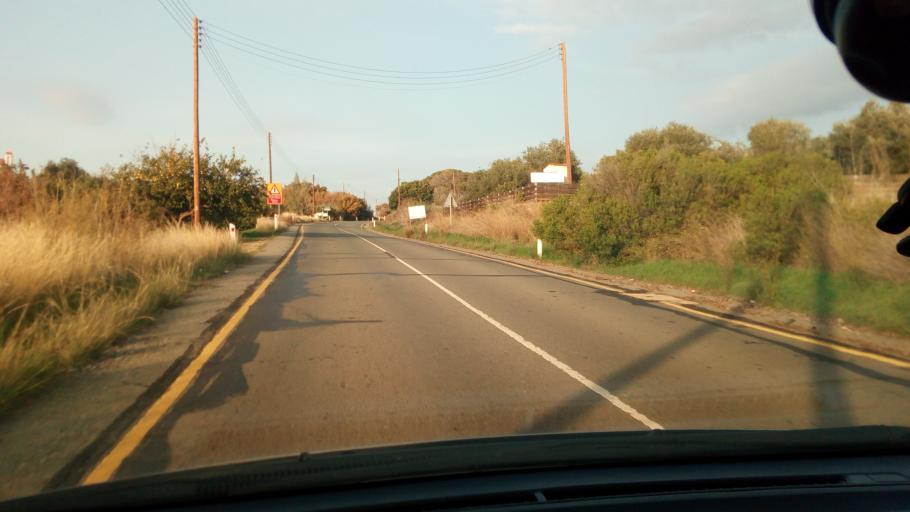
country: CY
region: Pafos
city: Polis
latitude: 35.1338
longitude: 32.5202
